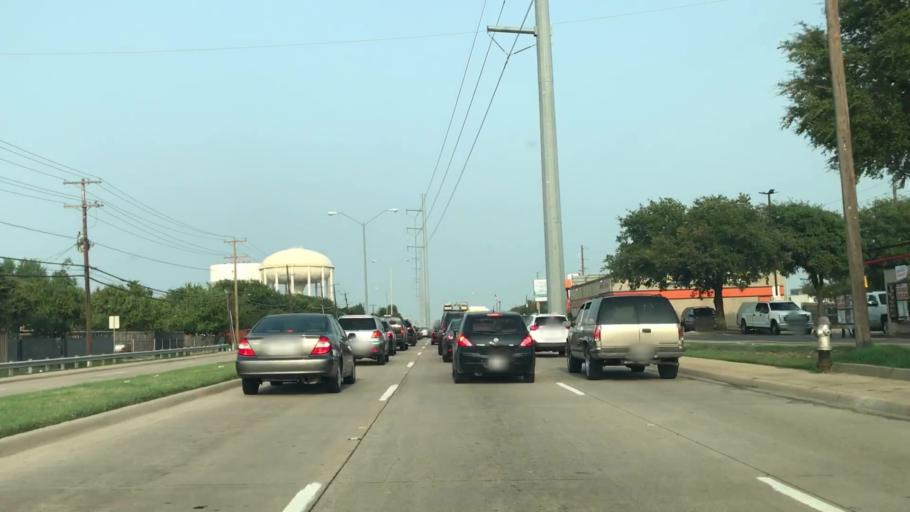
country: US
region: Texas
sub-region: Dallas County
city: Richardson
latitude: 32.9090
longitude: -96.7075
